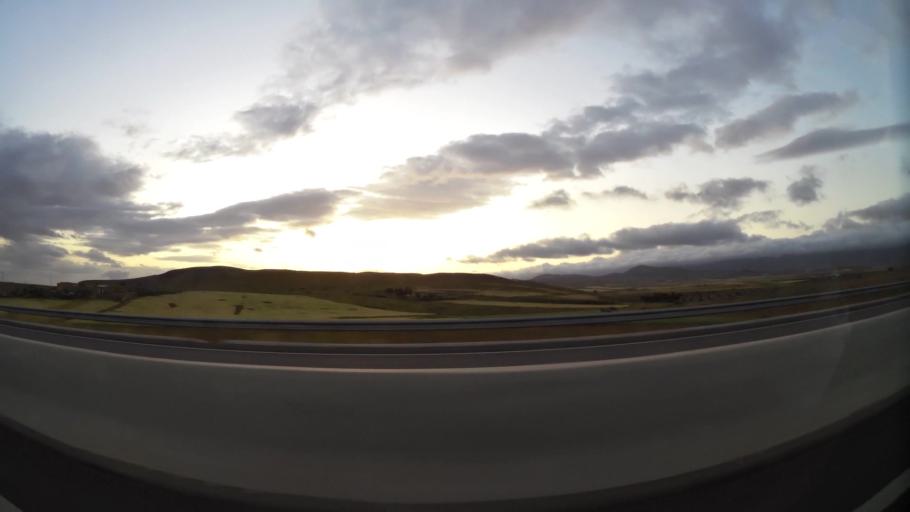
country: MA
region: Oriental
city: El Aioun
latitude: 34.6171
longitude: -2.5514
